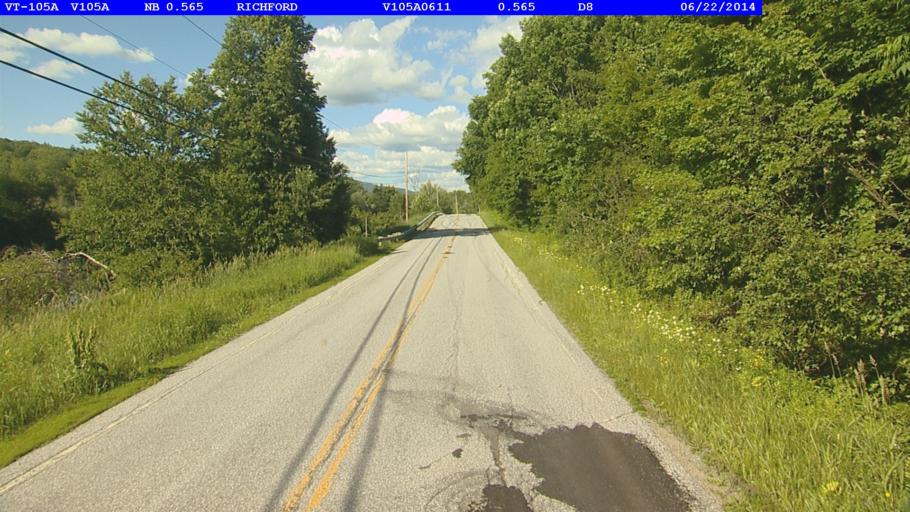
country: US
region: Vermont
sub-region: Franklin County
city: Richford
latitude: 45.0000
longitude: -72.6039
